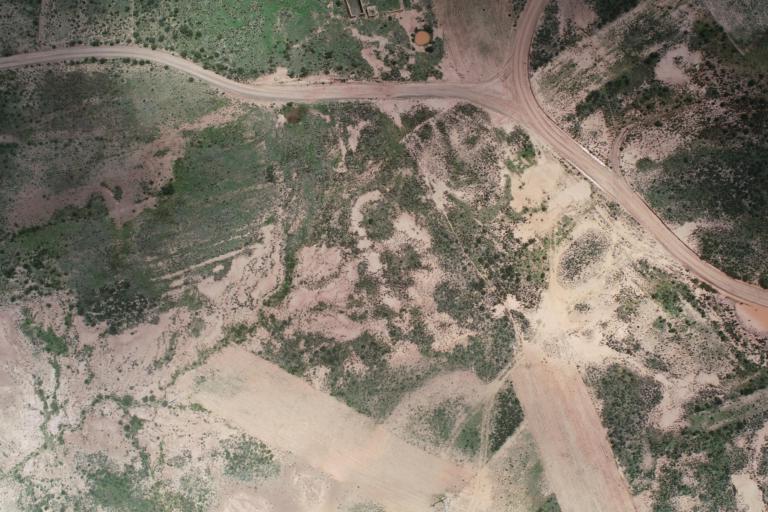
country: BO
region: La Paz
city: Curahuara de Carangas
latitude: -17.3246
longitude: -68.4990
